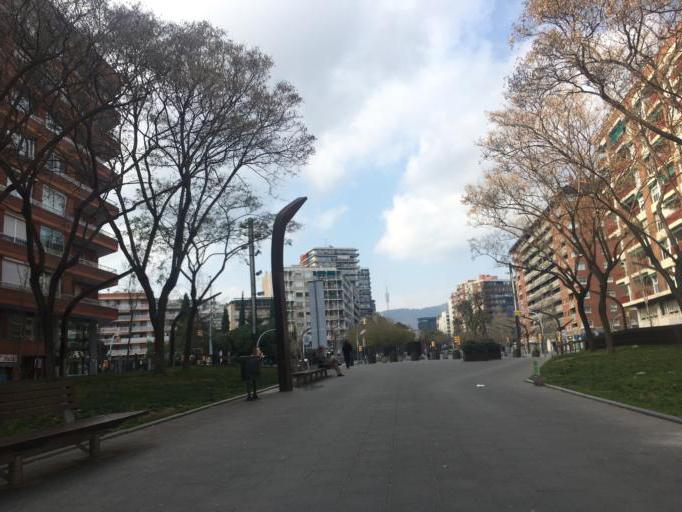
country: ES
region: Catalonia
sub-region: Provincia de Barcelona
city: les Corts
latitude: 41.3787
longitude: 2.1293
